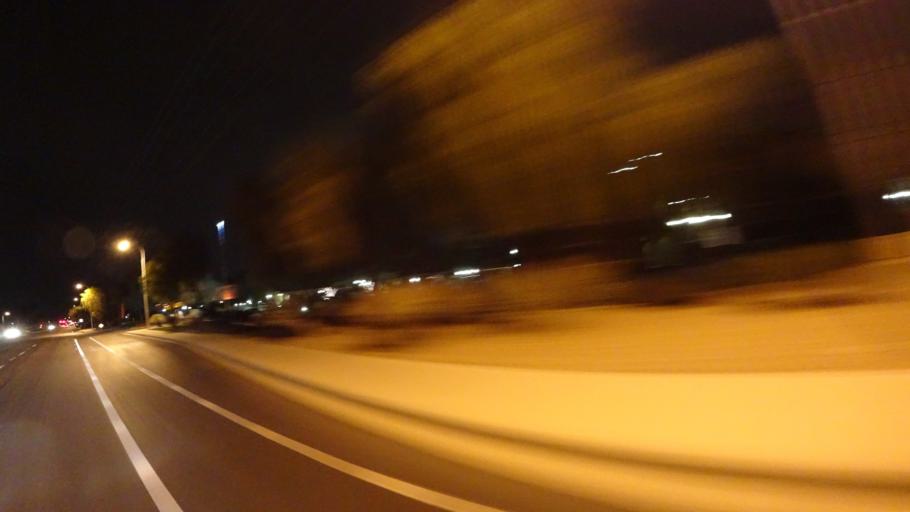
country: US
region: Arizona
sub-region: Maricopa County
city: Chandler
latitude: 33.2764
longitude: -111.8695
